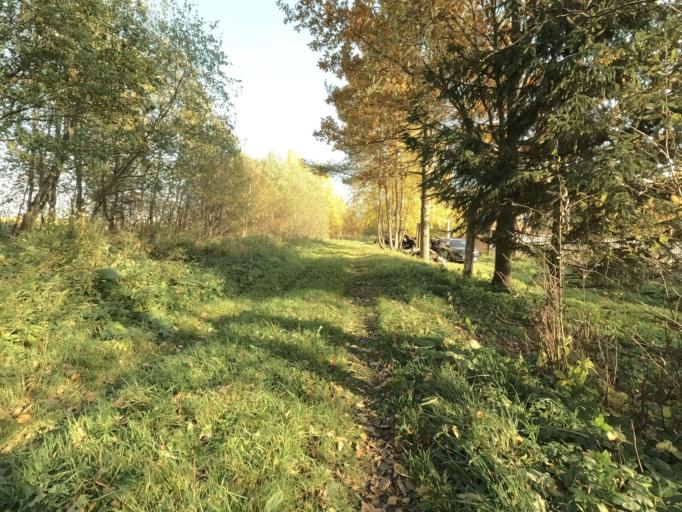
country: RU
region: Leningrad
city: Mga
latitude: 59.7474
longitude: 31.0733
